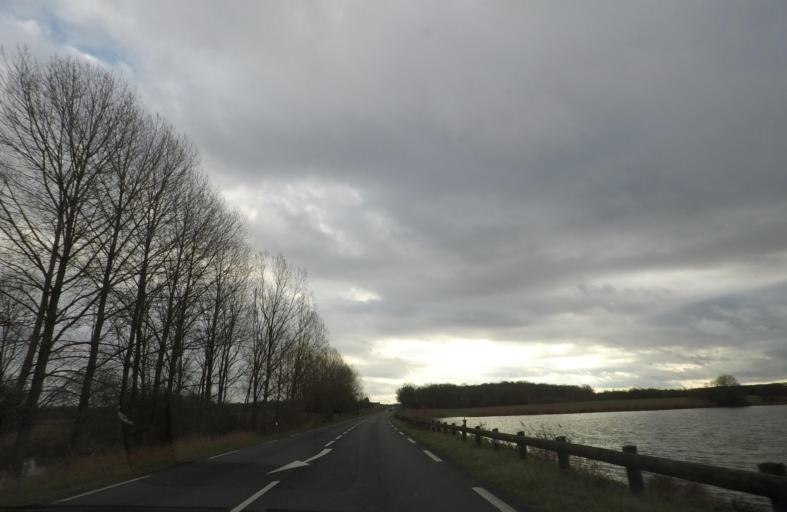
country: FR
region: Centre
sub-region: Departement du Loir-et-Cher
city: Soings-en-Sologne
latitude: 47.4359
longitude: 1.5573
